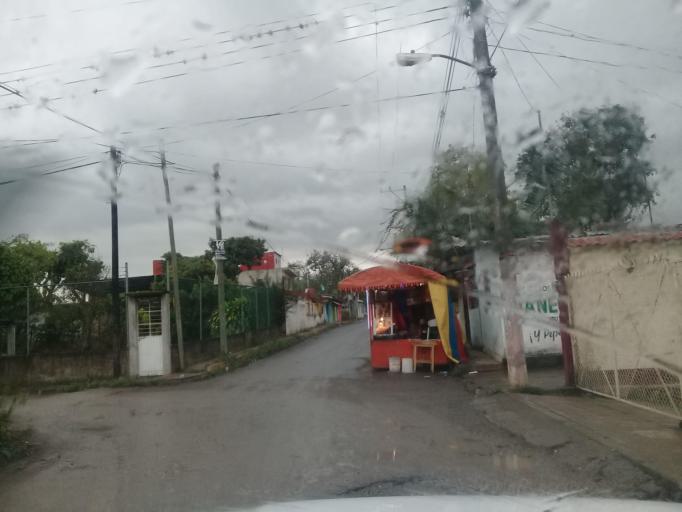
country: MX
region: Veracruz
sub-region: Cordoba
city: San Jose de Tapia
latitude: 18.8476
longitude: -96.9498
